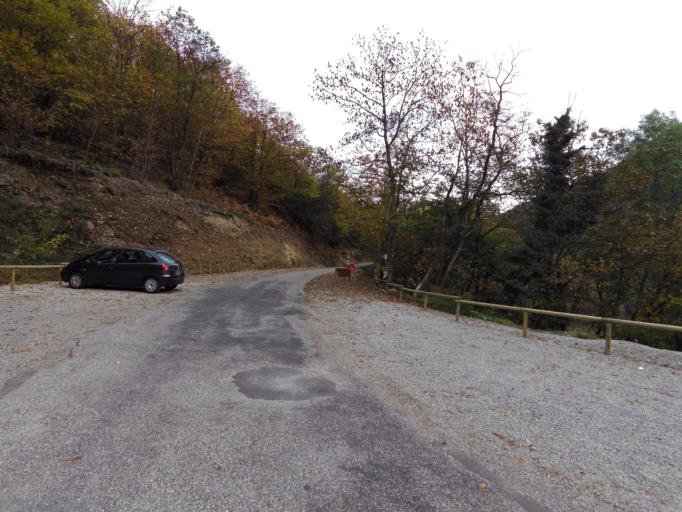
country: FR
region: Rhone-Alpes
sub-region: Departement de l'Ardeche
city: Les Vans
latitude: 44.4942
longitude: 4.0443
